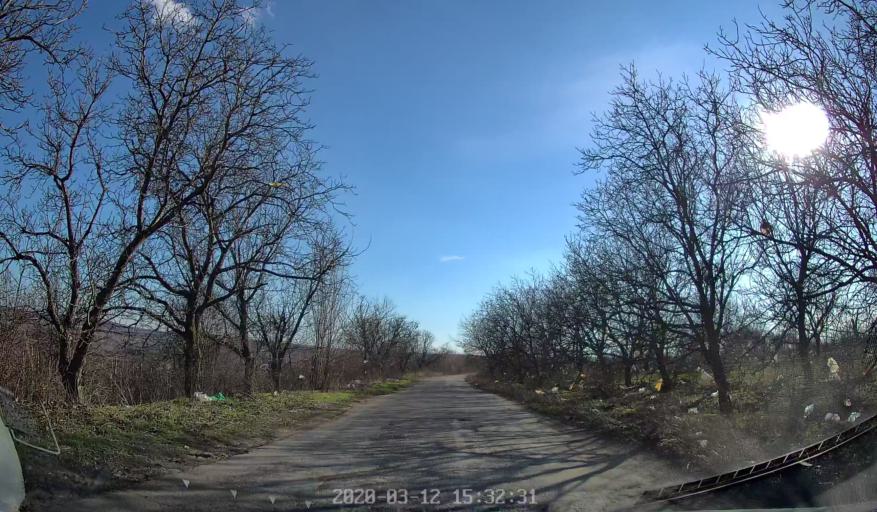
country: MD
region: Chisinau
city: Ciorescu
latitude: 47.1510
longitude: 28.9406
